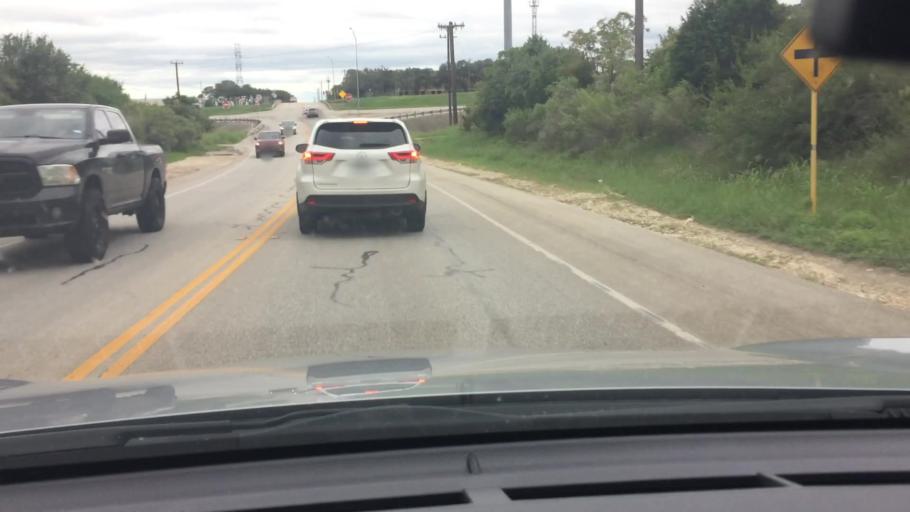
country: US
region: Texas
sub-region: Bexar County
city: Live Oak
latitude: 29.6047
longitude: -98.3671
